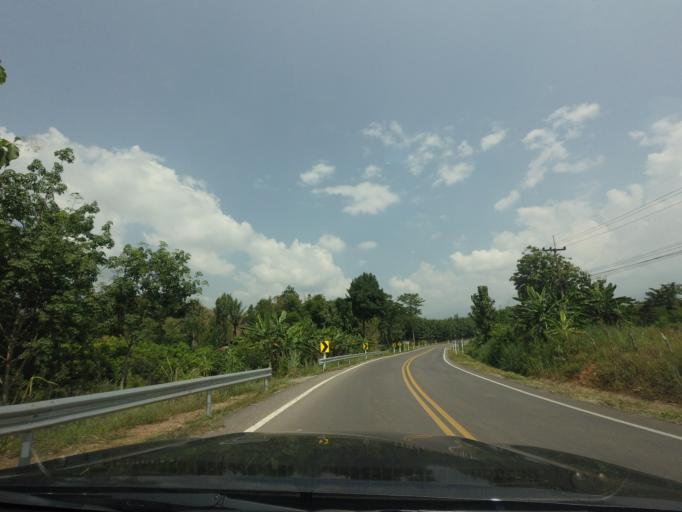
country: TH
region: Nan
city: Santi Suk
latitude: 18.9668
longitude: 100.9235
